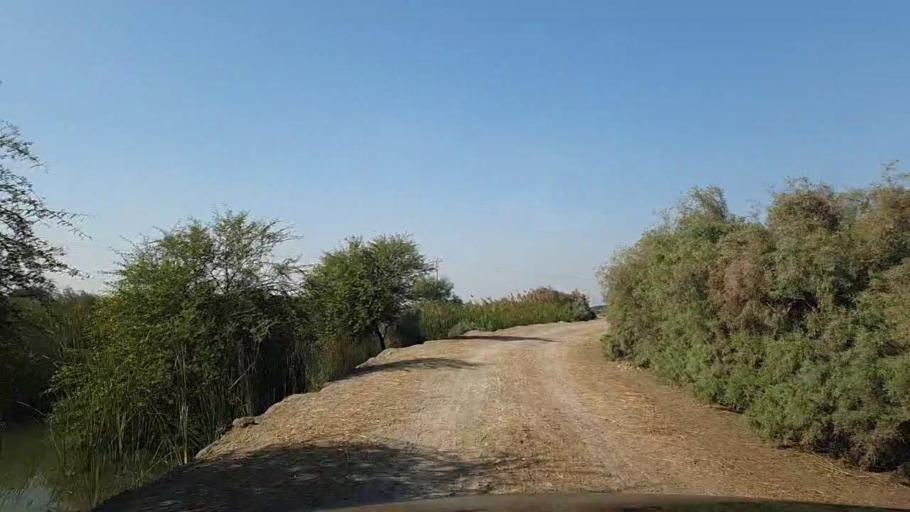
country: PK
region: Sindh
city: Mirpur Batoro
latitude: 24.7422
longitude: 68.3413
